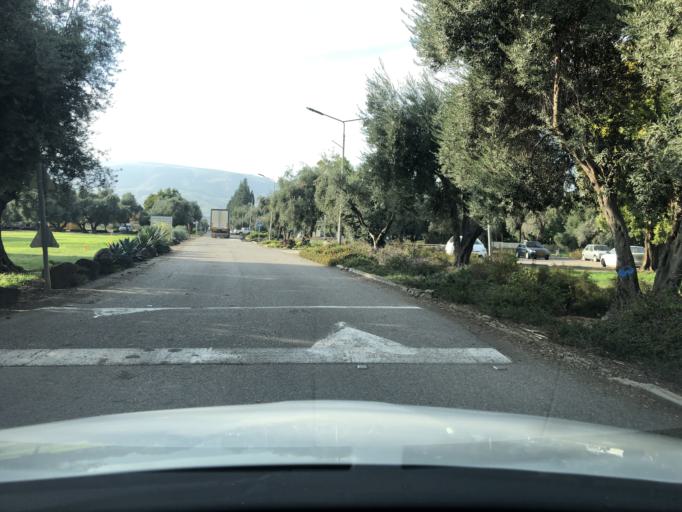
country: IL
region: Northern District
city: Yavne'el
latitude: 32.6579
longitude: 35.5794
